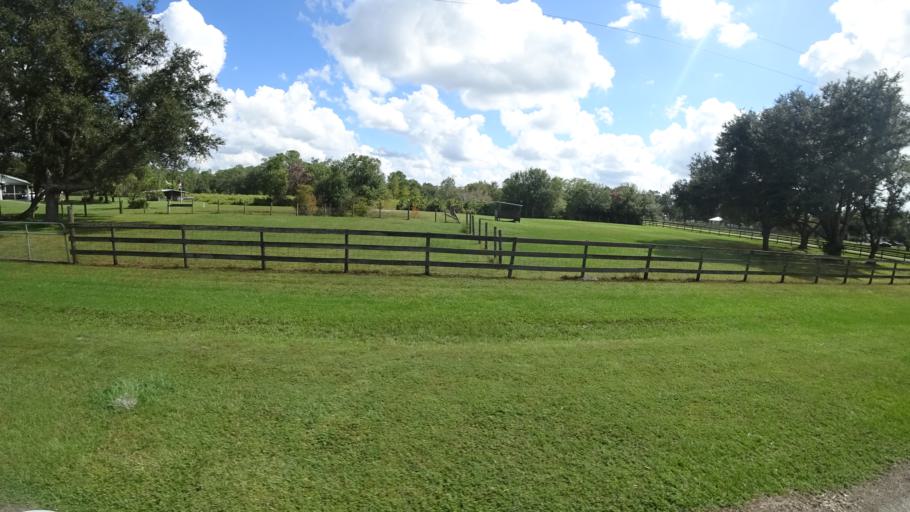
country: US
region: Florida
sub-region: Sarasota County
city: Lake Sarasota
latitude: 27.2808
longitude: -82.2242
